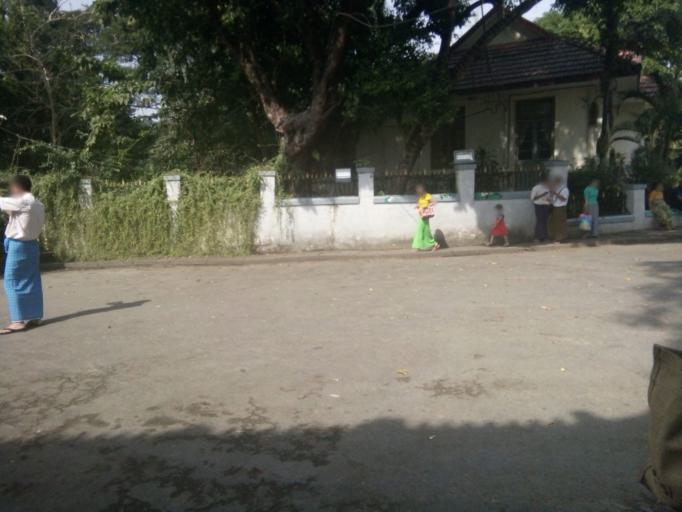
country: MM
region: Yangon
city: Yangon
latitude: 16.7948
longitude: 96.1588
